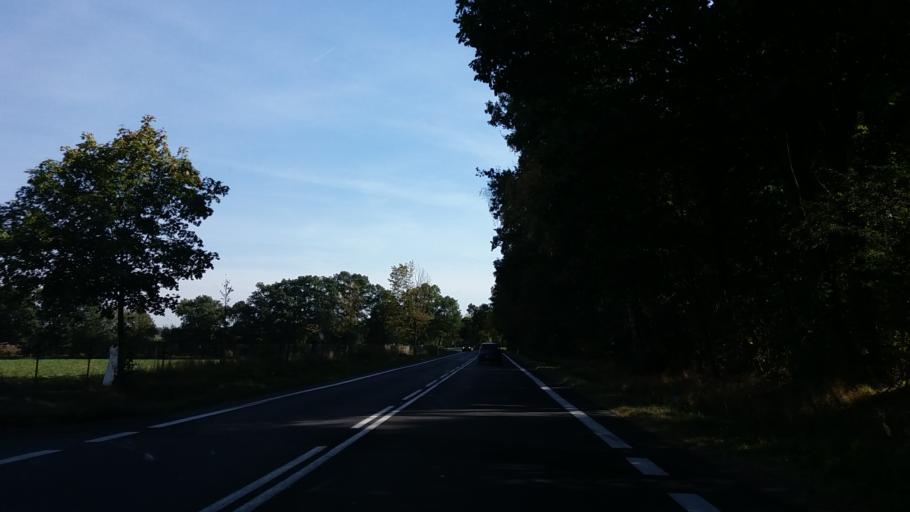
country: PL
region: Greater Poland Voivodeship
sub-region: Powiat miedzychodzki
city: Kwilcz
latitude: 52.5392
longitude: 16.1390
